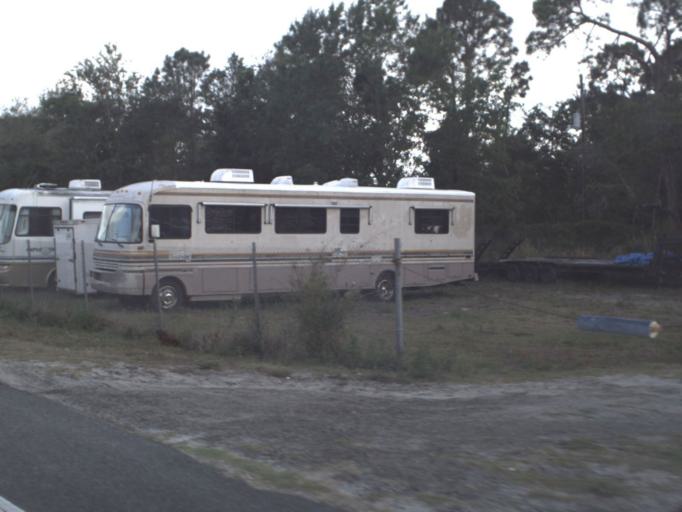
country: US
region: Florida
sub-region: Brevard County
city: Mims
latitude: 28.6996
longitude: -80.8596
